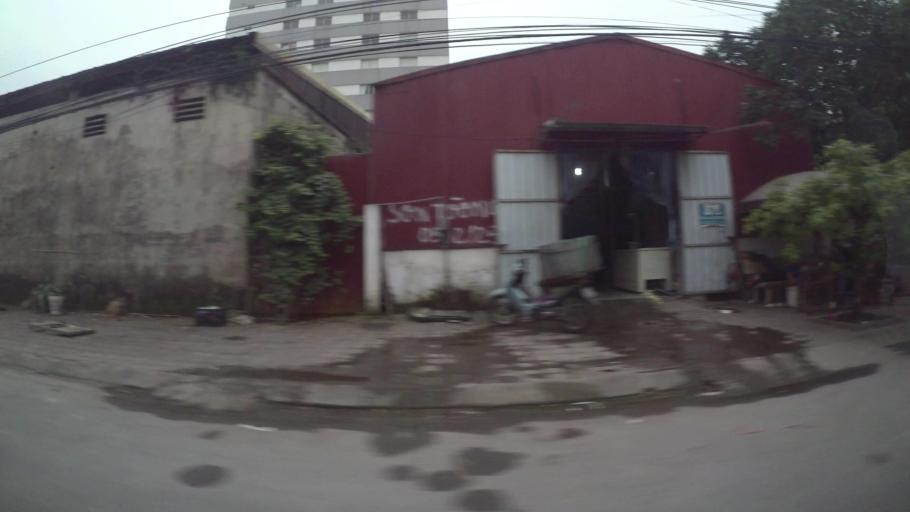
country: VN
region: Ha Noi
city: Trau Quy
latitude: 21.0358
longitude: 105.9042
